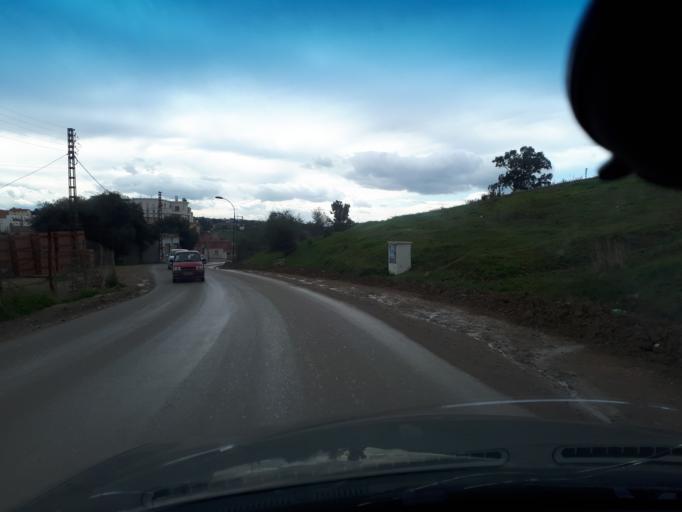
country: DZ
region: Tipaza
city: Douera
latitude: 36.7167
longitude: 2.9107
